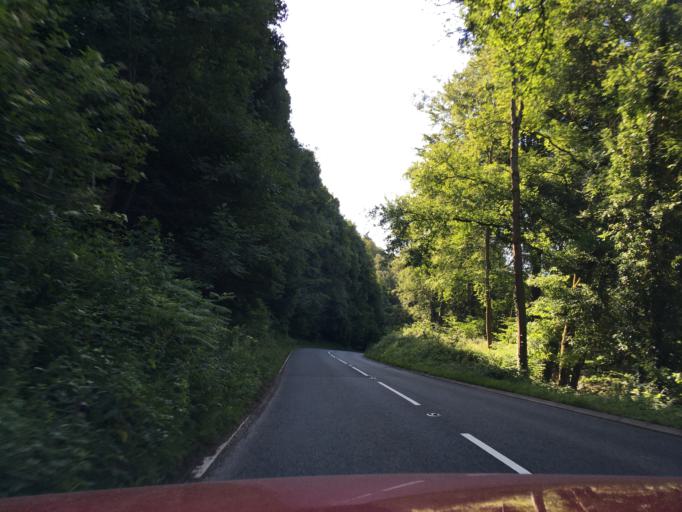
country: GB
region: England
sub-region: Gloucestershire
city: Lydney
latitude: 51.7399
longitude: -2.5403
